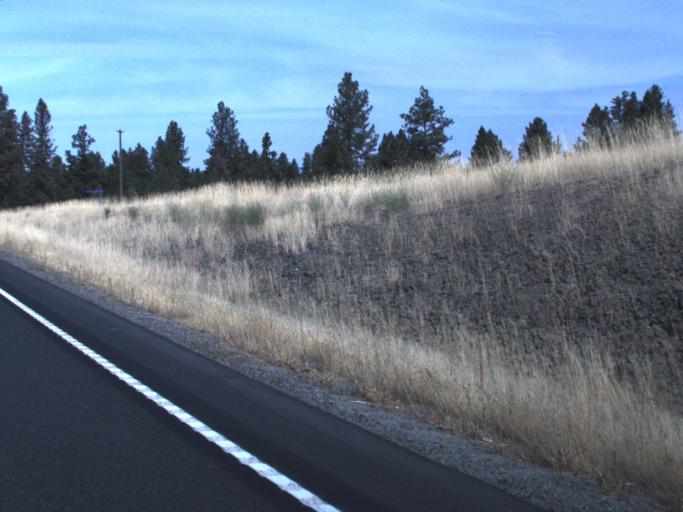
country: US
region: Washington
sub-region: Spokane County
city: Deer Park
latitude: 47.9063
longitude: -117.4423
